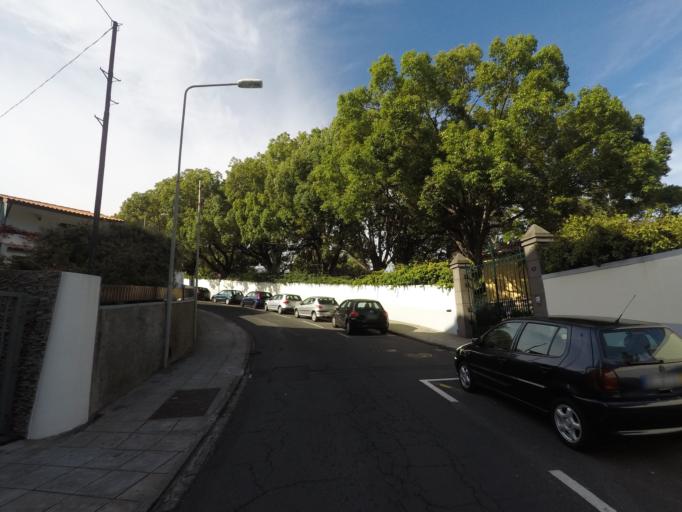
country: PT
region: Madeira
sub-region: Funchal
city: Funchal
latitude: 32.6408
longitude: -16.9274
